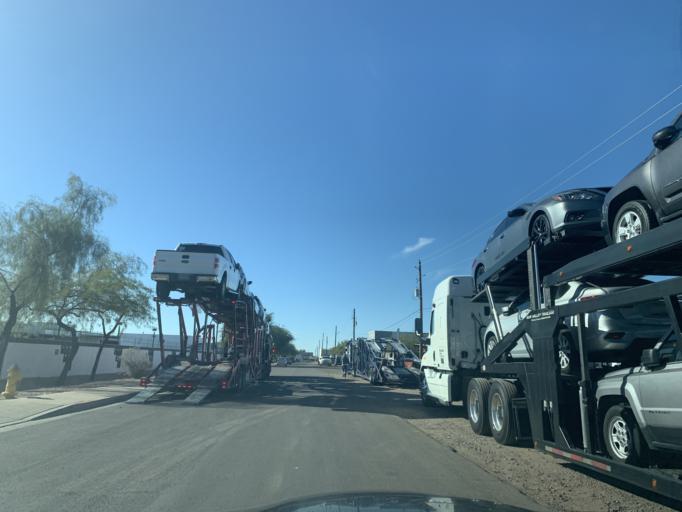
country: US
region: Arizona
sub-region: Maricopa County
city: Tempe Junction
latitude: 33.4183
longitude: -111.9827
